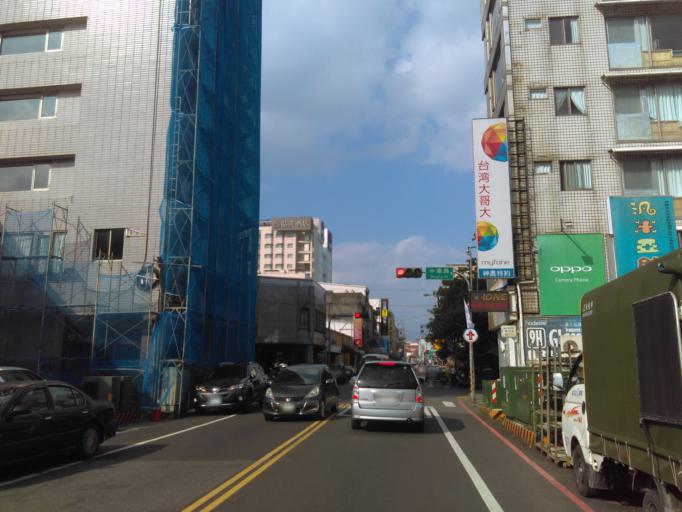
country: TW
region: Taiwan
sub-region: Yilan
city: Yilan
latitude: 24.7516
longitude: 121.7511
